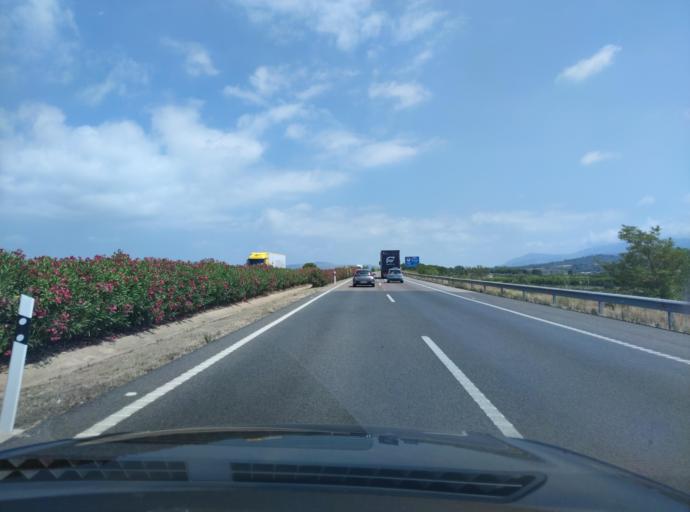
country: ES
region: Catalonia
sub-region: Provincia de Tarragona
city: Ulldecona
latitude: 40.5508
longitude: 0.4216
